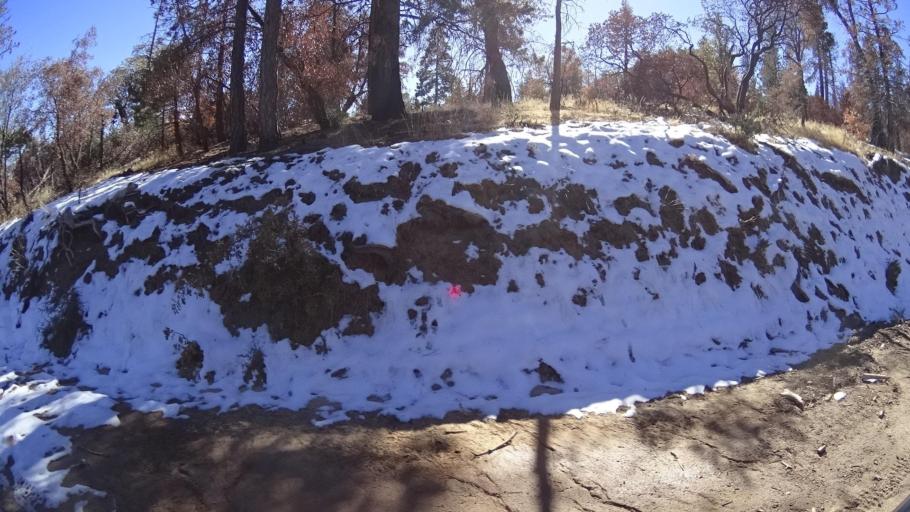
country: US
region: California
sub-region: Kern County
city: Alta Sierra
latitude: 35.7163
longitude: -118.5307
